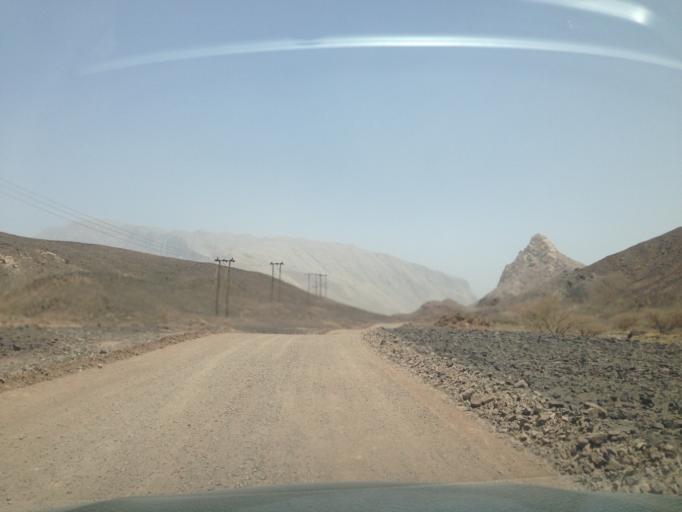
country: OM
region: Az Zahirah
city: `Ibri
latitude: 23.1972
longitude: 56.8827
